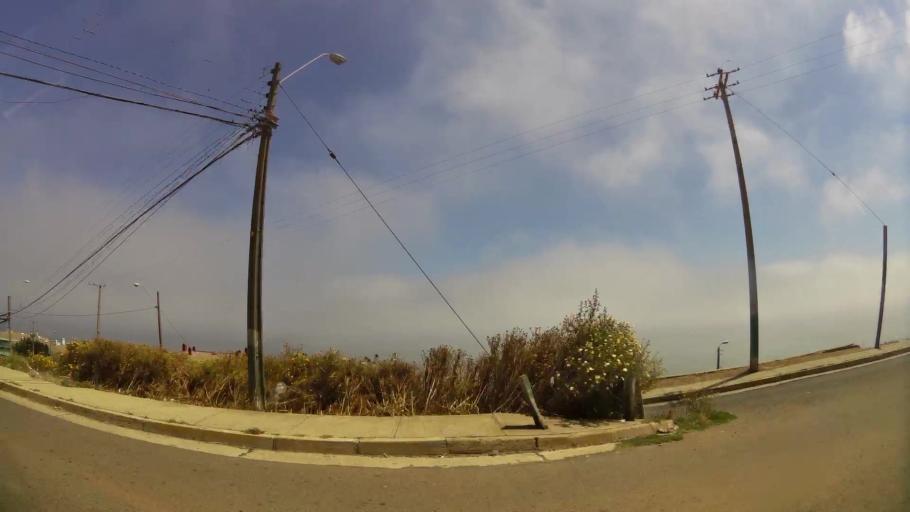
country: CL
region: Valparaiso
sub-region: Provincia de Valparaiso
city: Valparaiso
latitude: -33.0286
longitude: -71.6499
